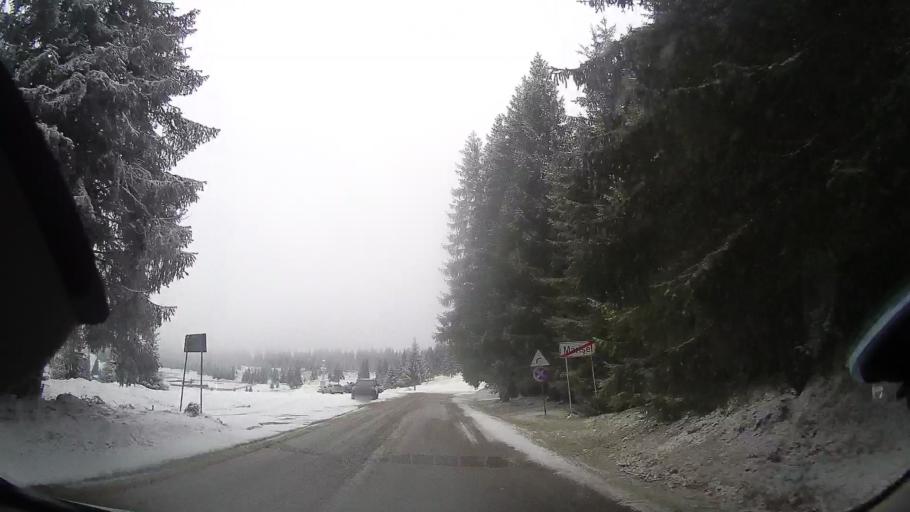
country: RO
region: Cluj
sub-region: Comuna Belis
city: Belis
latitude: 46.6373
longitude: 23.0462
